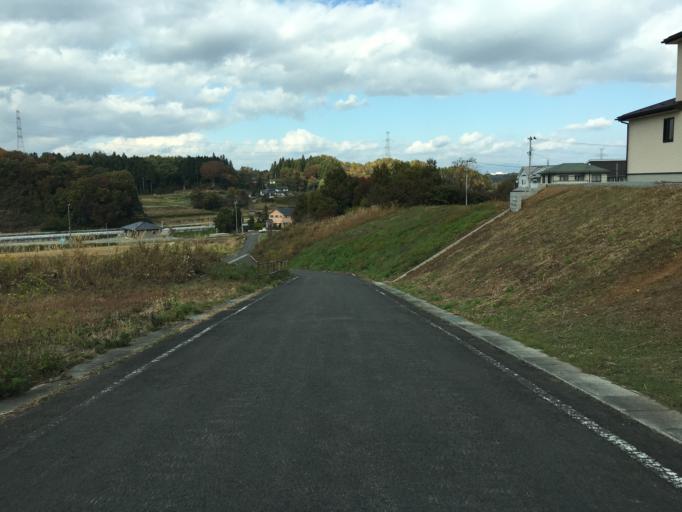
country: JP
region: Fukushima
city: Fukushima-shi
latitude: 37.6661
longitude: 140.4653
